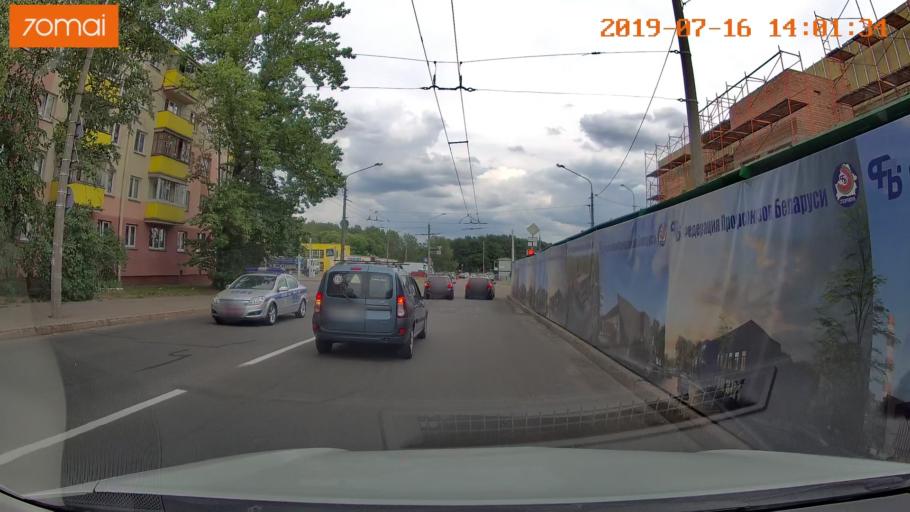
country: BY
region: Minsk
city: Minsk
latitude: 53.9289
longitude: 27.5646
